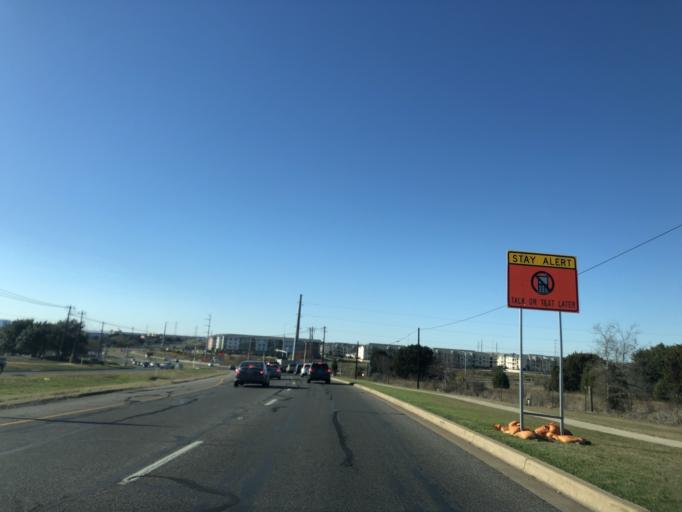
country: US
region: Texas
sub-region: Travis County
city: Wells Branch
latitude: 30.4047
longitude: -97.6620
